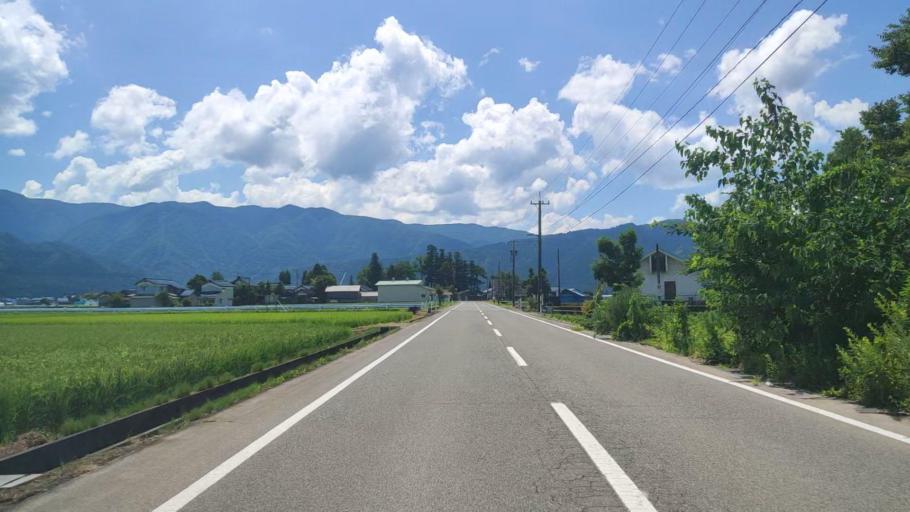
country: JP
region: Fukui
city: Ono
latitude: 35.9636
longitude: 136.5301
